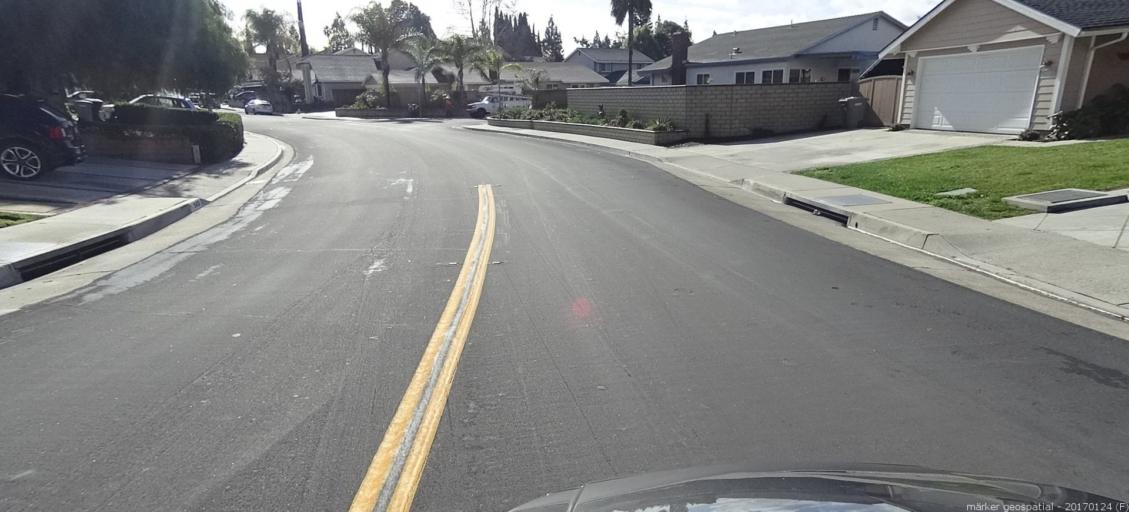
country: US
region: California
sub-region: Orange County
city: Laguna Hills
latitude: 33.6280
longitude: -117.7108
